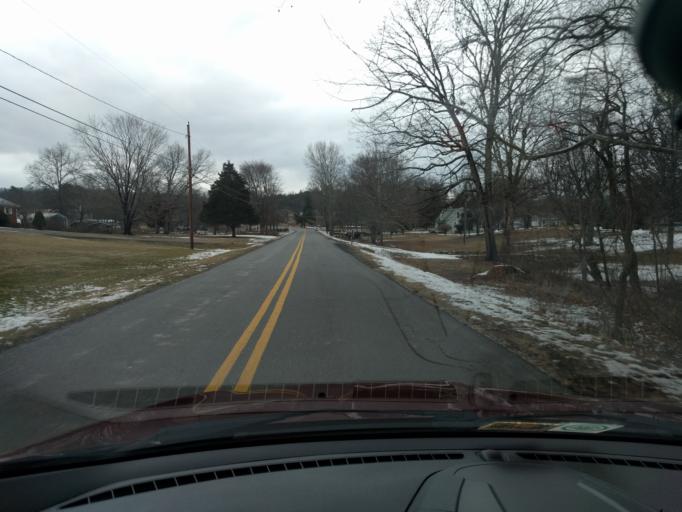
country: US
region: Virginia
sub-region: Alleghany County
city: Clifton Forge
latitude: 37.8371
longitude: -79.7453
